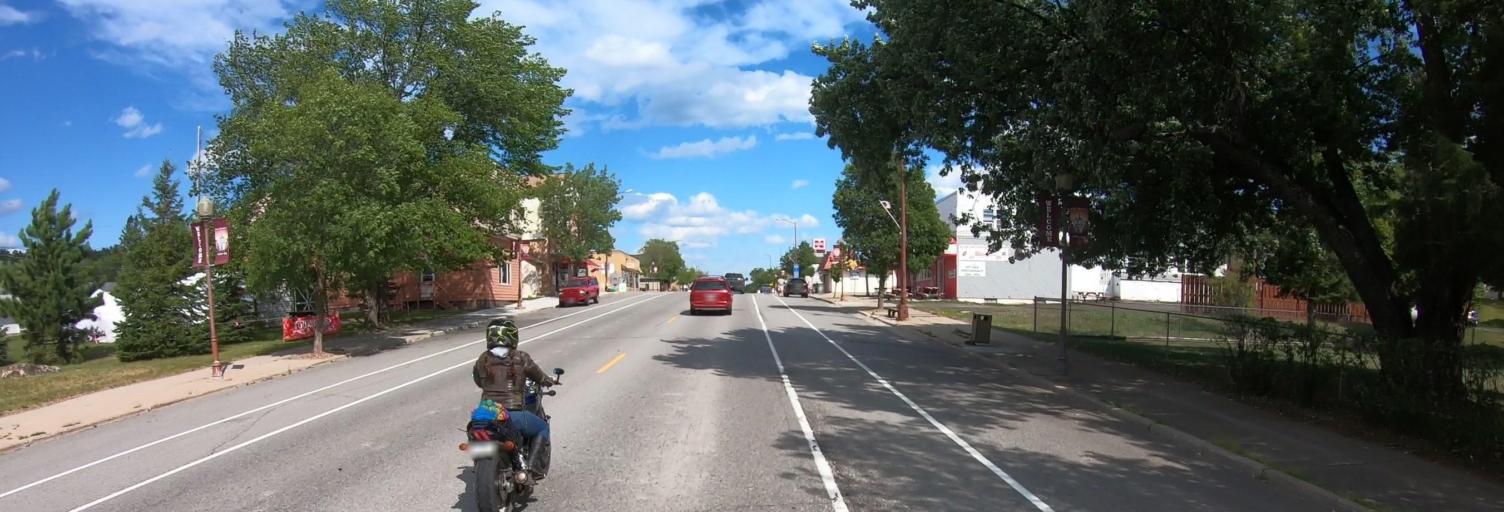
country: US
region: Minnesota
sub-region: Saint Louis County
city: Aurora
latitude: 47.8053
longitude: -92.2780
